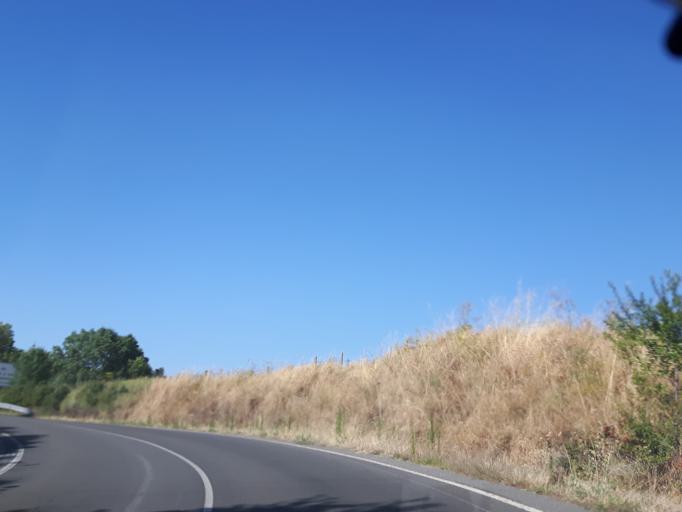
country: ES
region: Castille and Leon
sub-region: Provincia de Salamanca
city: Navalmoral de Bejar
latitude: 40.4100
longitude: -5.8092
